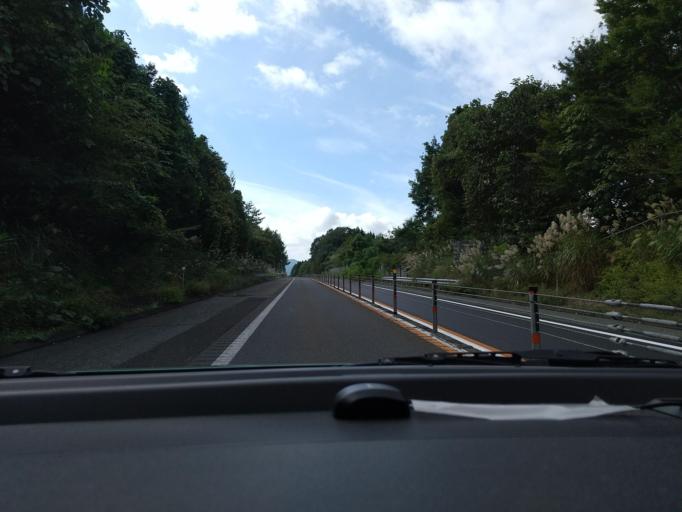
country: JP
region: Iwate
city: Kitakami
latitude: 39.2805
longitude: 141.0338
